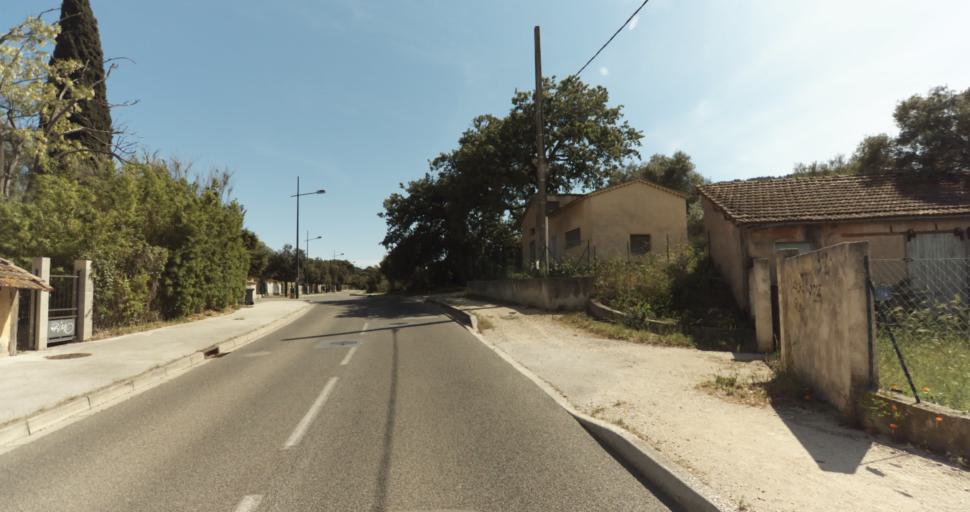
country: FR
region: Provence-Alpes-Cote d'Azur
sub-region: Departement du Var
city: Hyeres
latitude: 43.1016
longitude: 6.1211
